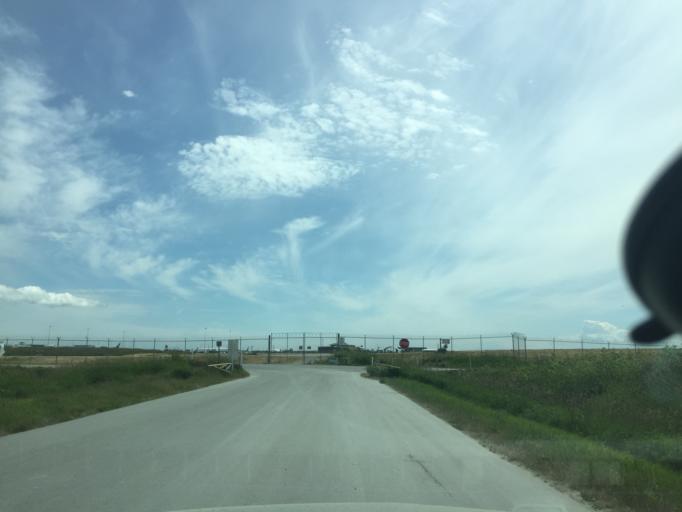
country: CA
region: British Columbia
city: Richmond
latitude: 49.2073
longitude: -123.1922
